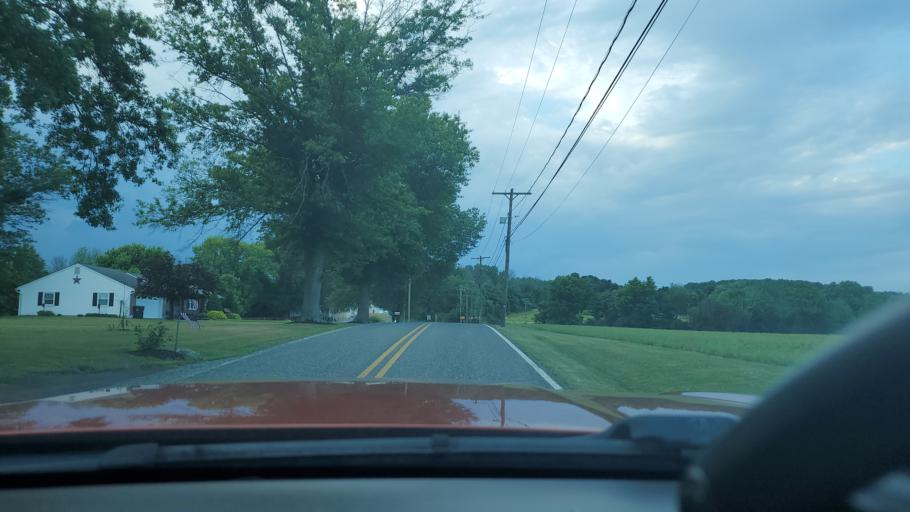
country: US
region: Pennsylvania
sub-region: Montgomery County
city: Limerick
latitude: 40.2497
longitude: -75.5213
